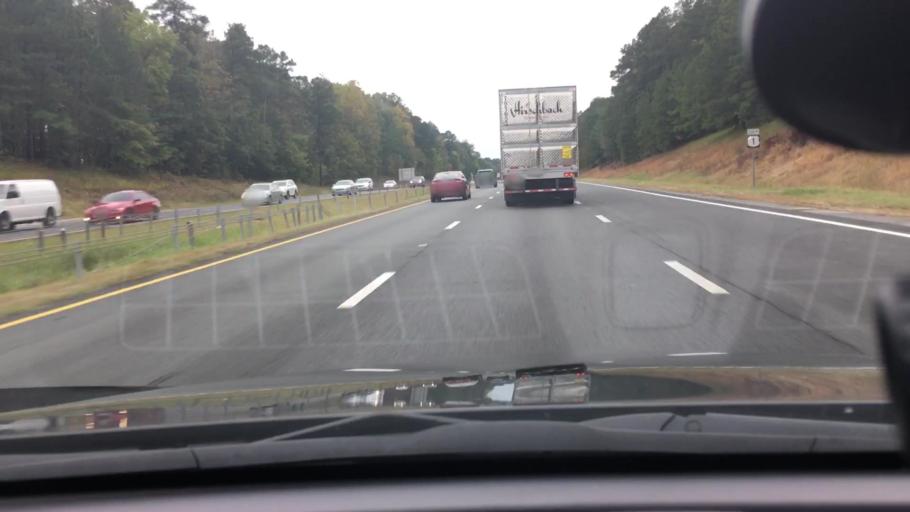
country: US
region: North Carolina
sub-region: Wake County
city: Apex
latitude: 35.7330
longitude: -78.8011
